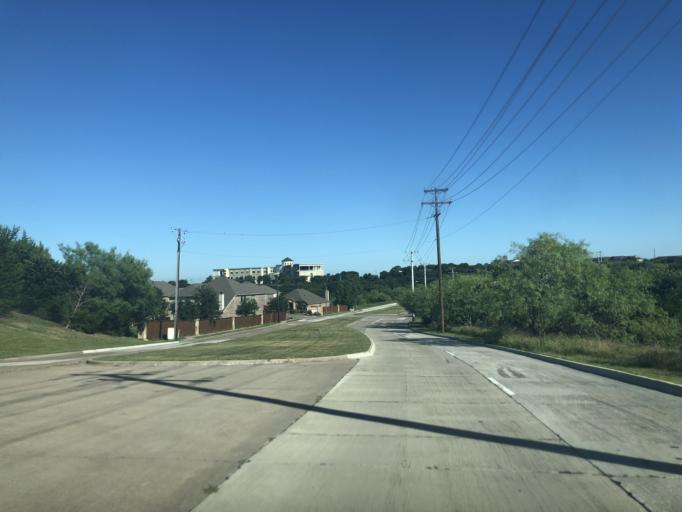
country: US
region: Texas
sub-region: Dallas County
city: Duncanville
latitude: 32.6584
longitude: -96.9620
